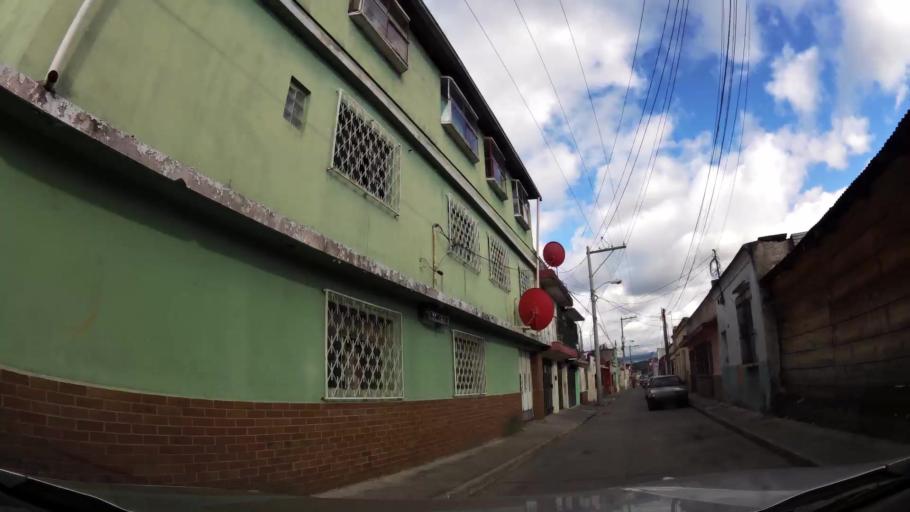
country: GT
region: Guatemala
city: Guatemala City
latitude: 14.6368
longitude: -90.5024
